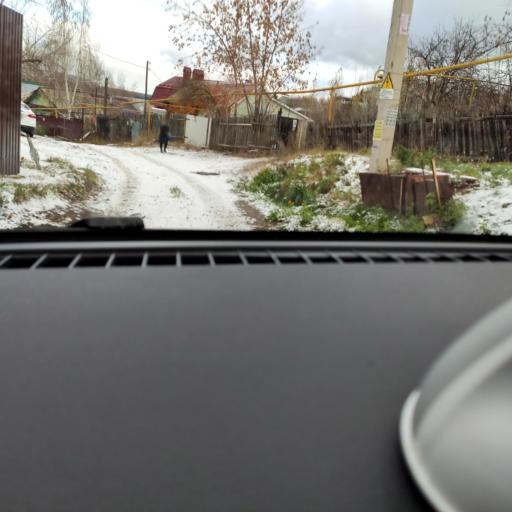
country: RU
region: Samara
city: Samara
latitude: 53.2275
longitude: 50.1548
